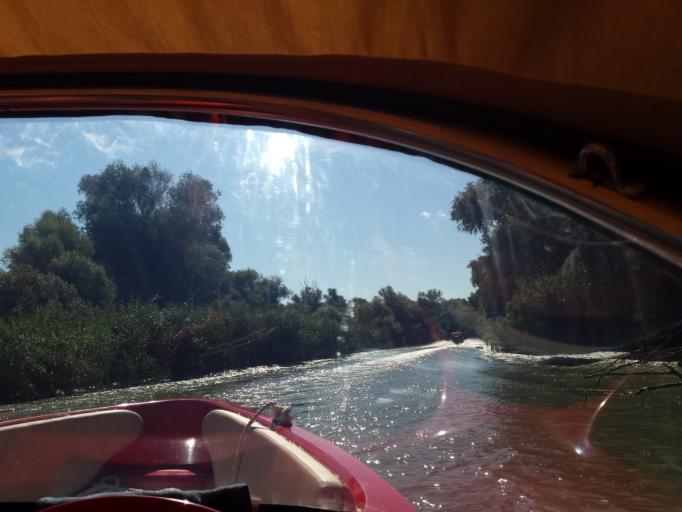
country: RO
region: Tulcea
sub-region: Comuna Pardina
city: Pardina
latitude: 45.2476
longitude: 29.0190
